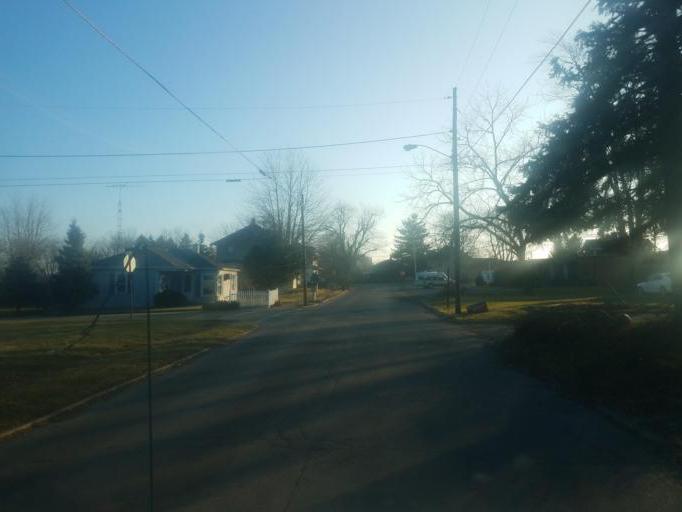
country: US
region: Ohio
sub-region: Crawford County
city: Bucyrus
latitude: 40.8196
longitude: -82.9660
